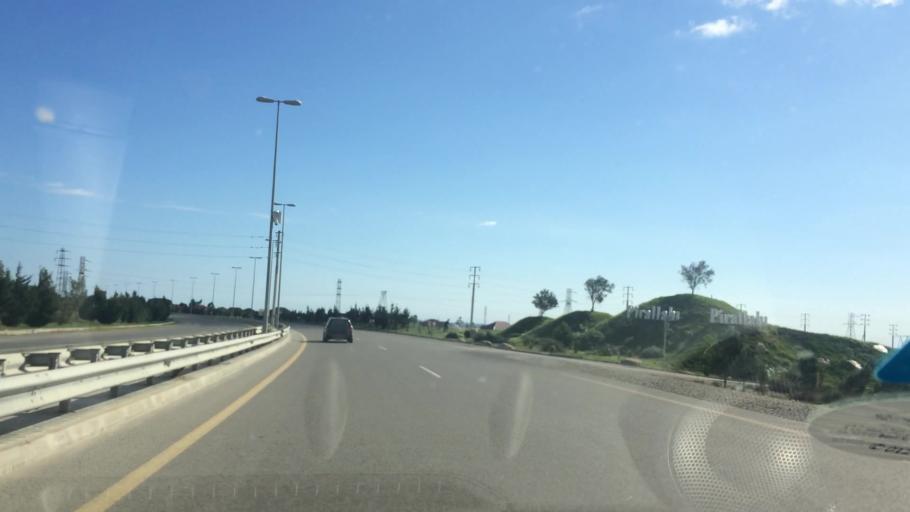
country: AZ
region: Baki
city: Zyrya
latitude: 40.3992
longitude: 50.3267
